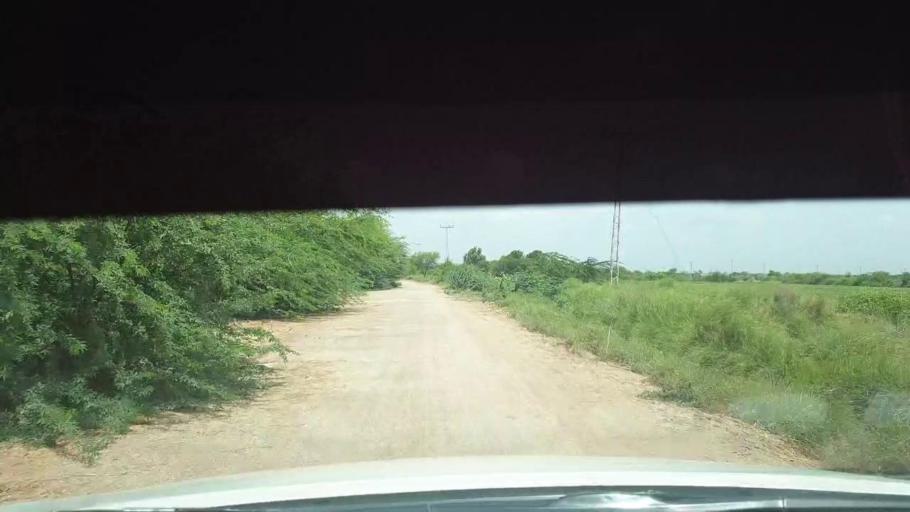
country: PK
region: Sindh
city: Kadhan
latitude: 24.5152
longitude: 68.9729
